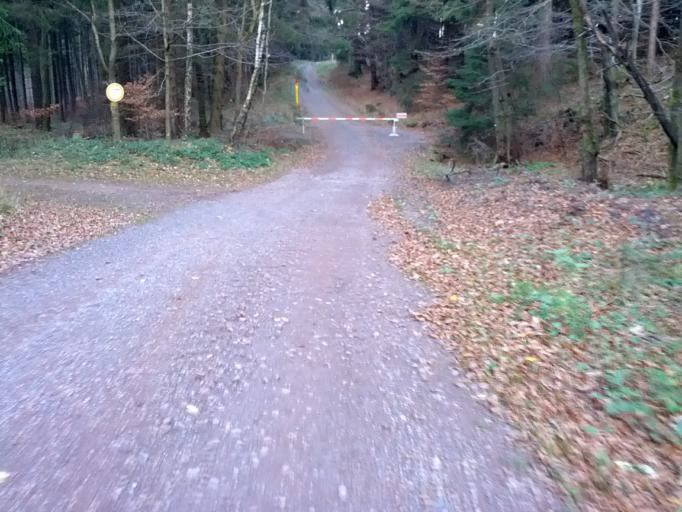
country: DE
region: Thuringia
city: Seebach
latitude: 50.8724
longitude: 10.4104
